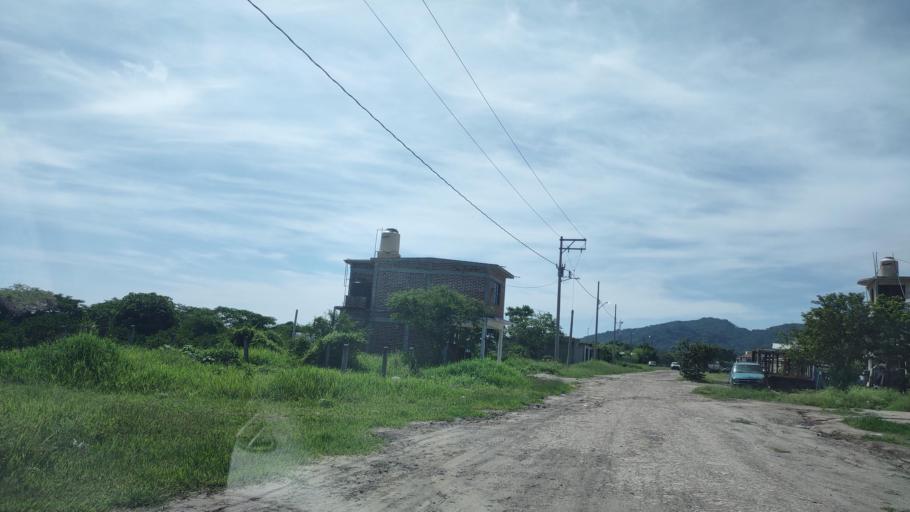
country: MX
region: Veracruz
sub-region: Emiliano Zapata
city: Dos Rios
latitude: 19.4291
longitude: -96.7994
